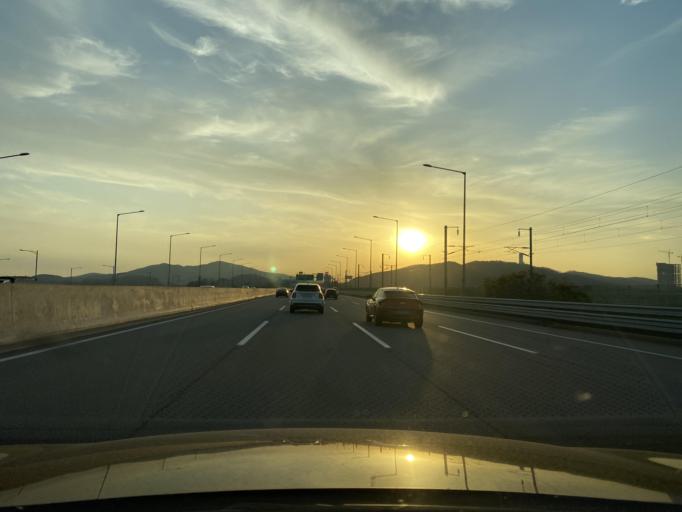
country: KR
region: Incheon
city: Incheon
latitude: 37.5259
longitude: 126.5475
